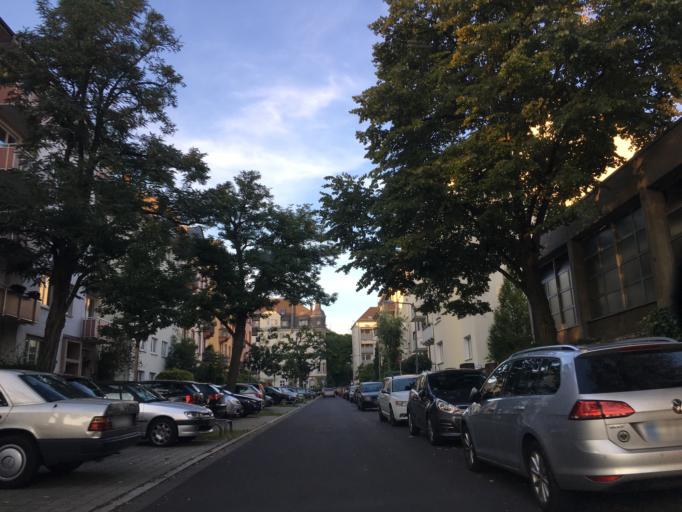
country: DE
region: Hesse
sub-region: Regierungsbezirk Darmstadt
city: Frankfurt am Main
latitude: 50.1192
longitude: 8.7067
